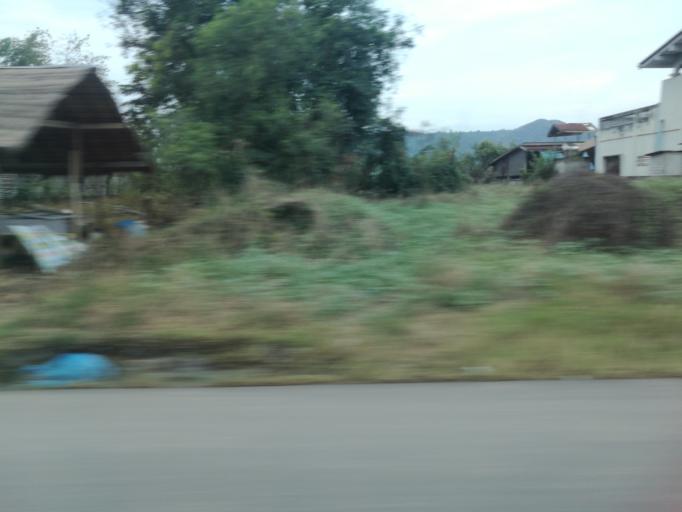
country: TH
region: Prachuap Khiri Khan
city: Sam Roi Yot
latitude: 12.2922
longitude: 99.8739
